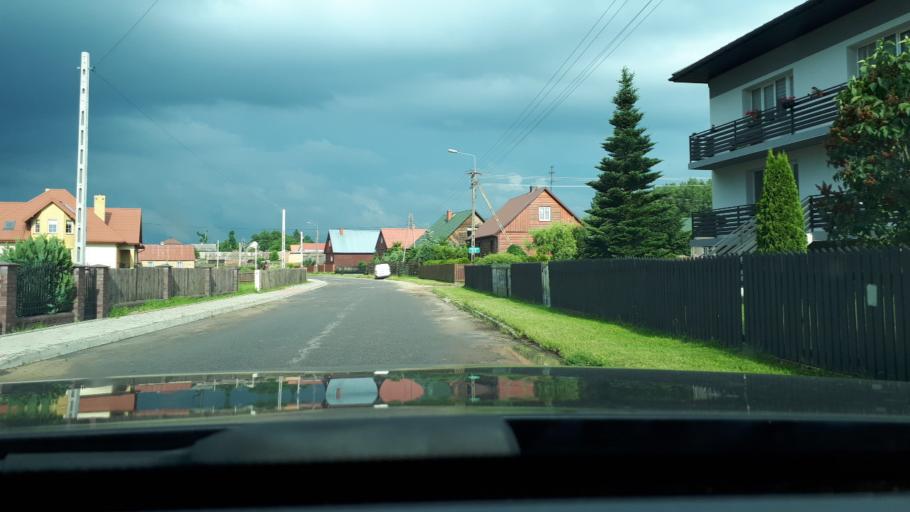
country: PL
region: Podlasie
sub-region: Powiat moniecki
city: Knyszyn
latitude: 53.2731
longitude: 22.9796
